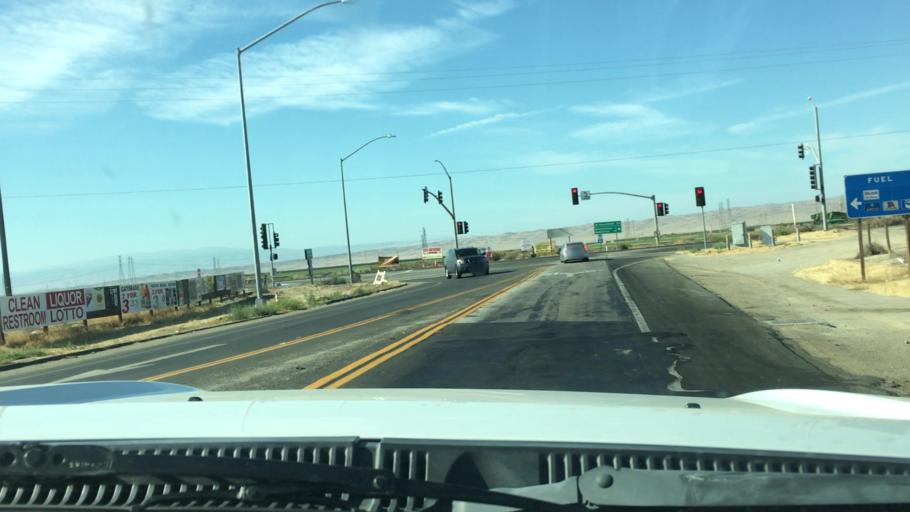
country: US
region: California
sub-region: Kern County
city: Buttonwillow
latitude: 35.3998
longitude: -119.4005
